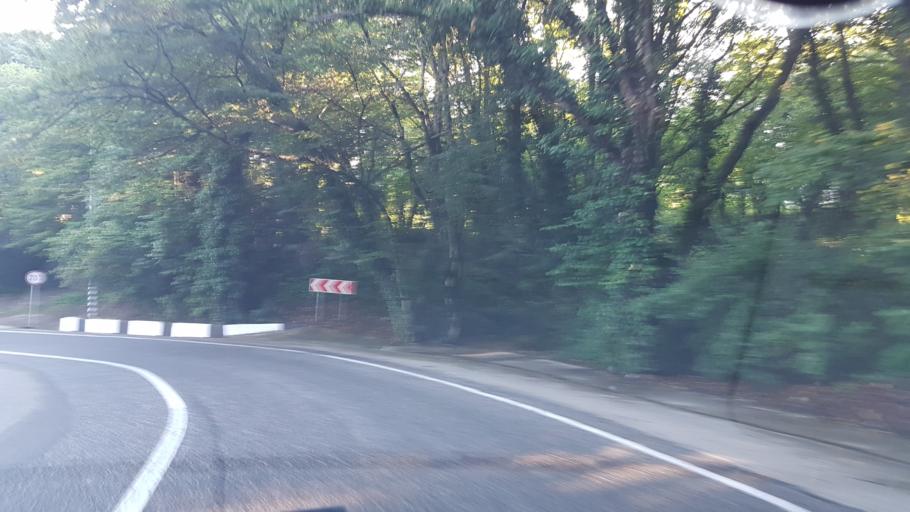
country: RU
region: Krasnodarskiy
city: Gornoye Loo
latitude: 43.6713
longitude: 39.6214
